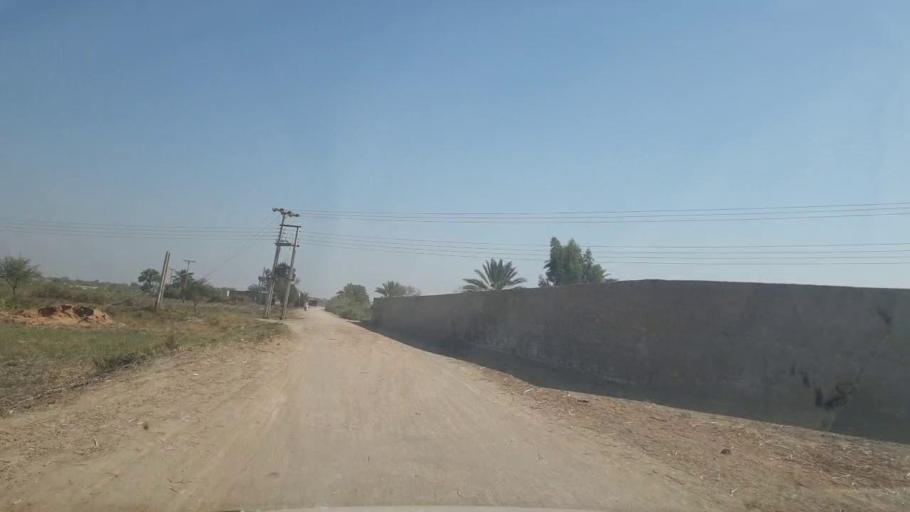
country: PK
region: Sindh
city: Mirpur Khas
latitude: 25.5180
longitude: 69.1814
